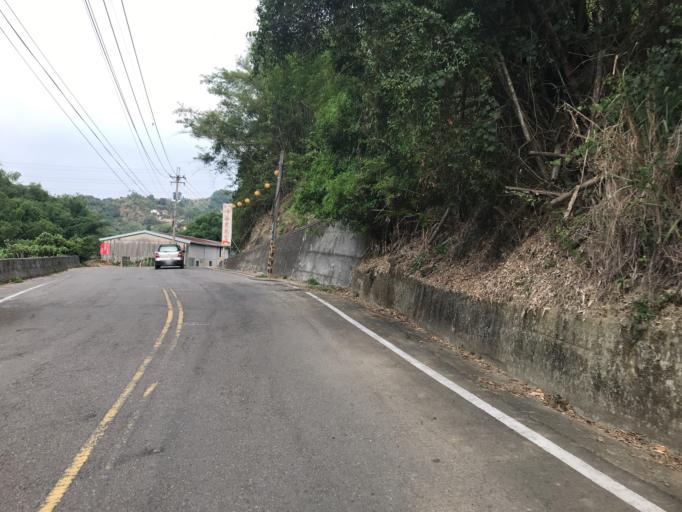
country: TW
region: Taiwan
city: Zhongxing New Village
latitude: 24.0386
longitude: 120.7090
